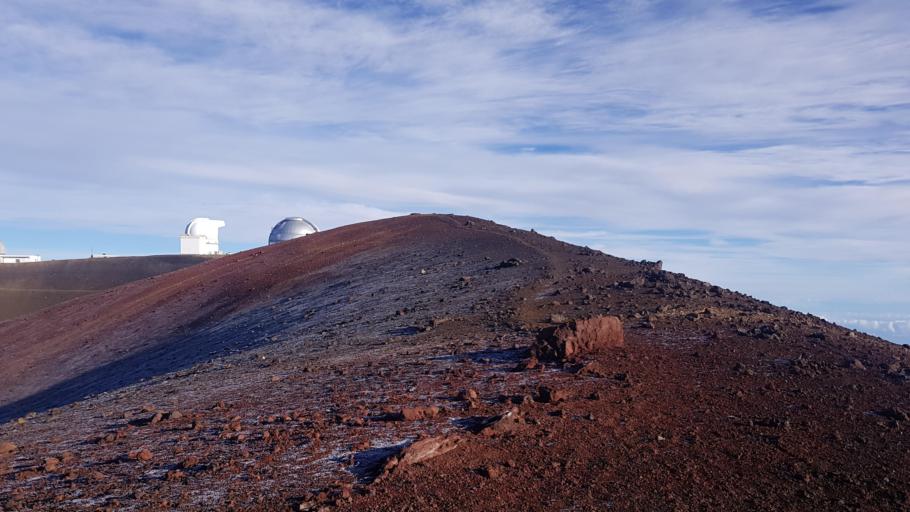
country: US
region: Hawaii
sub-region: Hawaii County
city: Honoka'a
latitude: 19.8191
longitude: -155.4681
